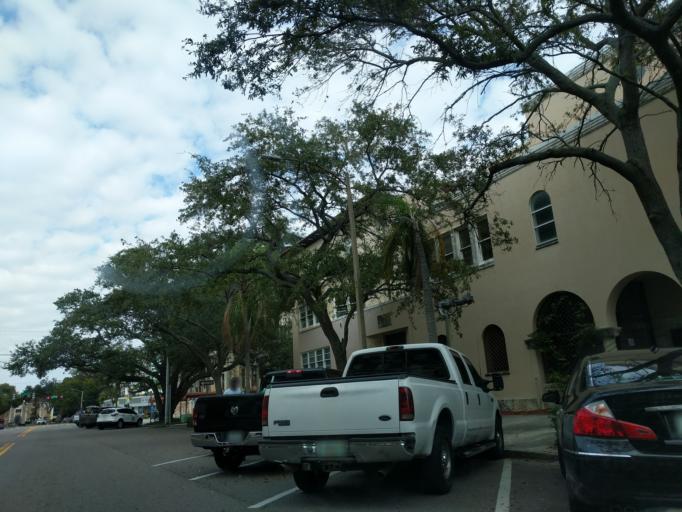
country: US
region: Florida
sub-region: Pinellas County
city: Saint Petersburg
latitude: 27.7724
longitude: -82.6402
